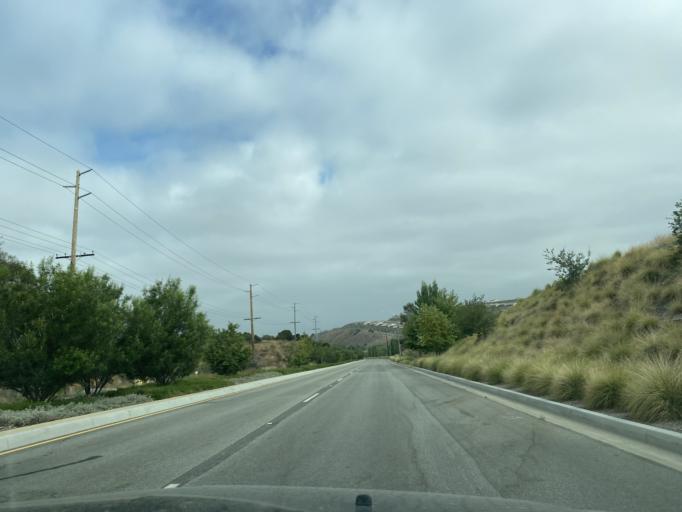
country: US
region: California
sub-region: Riverside County
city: El Cerrito
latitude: 33.7554
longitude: -117.4556
